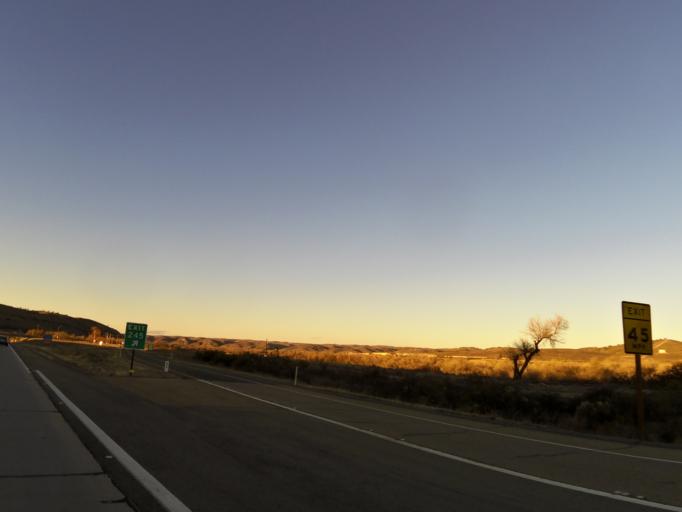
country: US
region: California
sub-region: San Luis Obispo County
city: San Miguel
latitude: 35.8118
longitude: -120.7525
